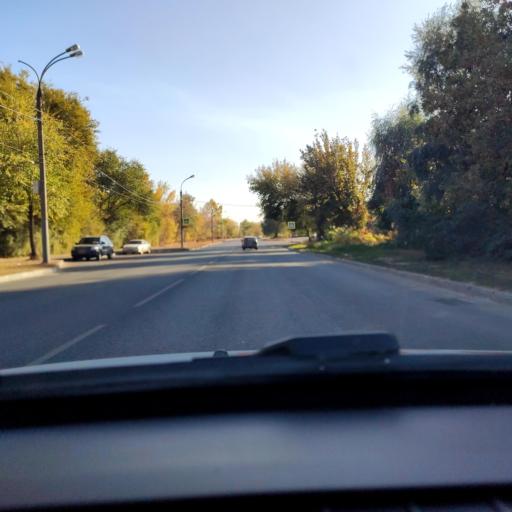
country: RU
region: Voronezj
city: Voronezh
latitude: 51.6420
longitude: 39.2108
